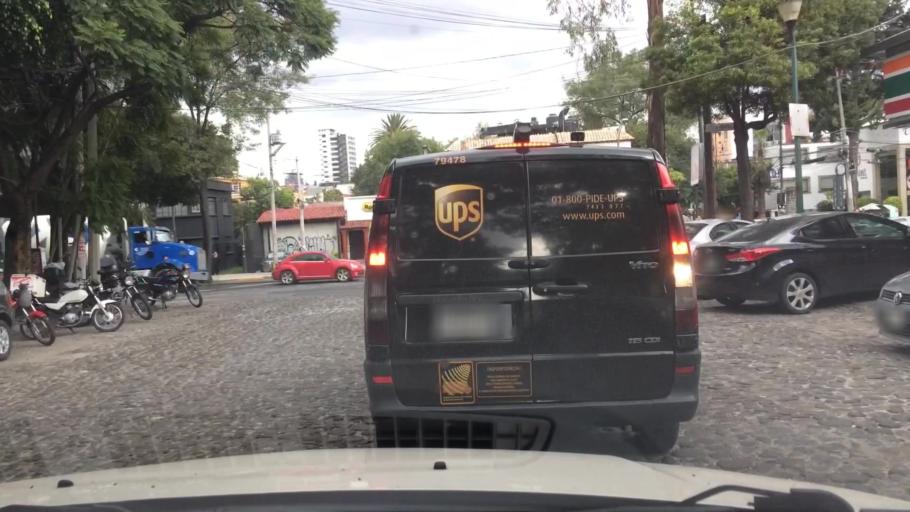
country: MX
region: Mexico City
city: Alvaro Obregon
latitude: 19.3576
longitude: -99.1901
